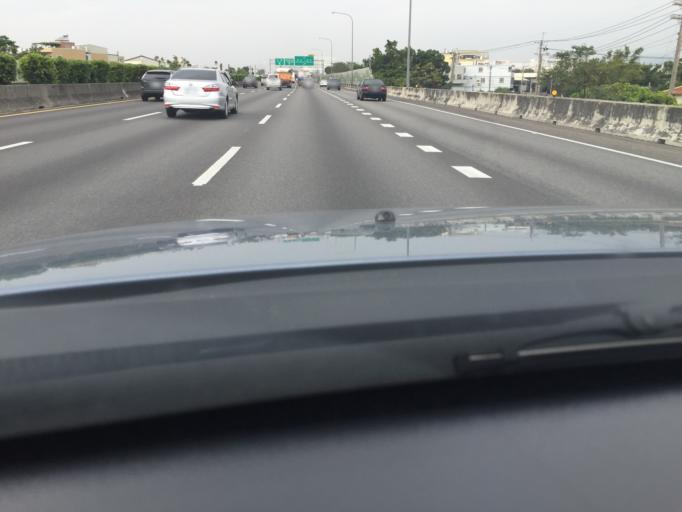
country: TW
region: Taiwan
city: Fengyuan
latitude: 24.2403
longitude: 120.6891
